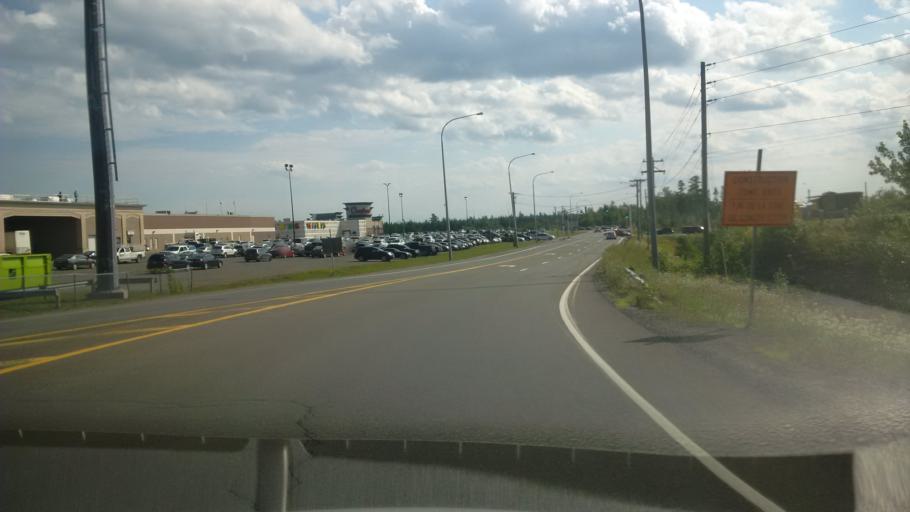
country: CA
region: New Brunswick
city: Fredericton
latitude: 45.9379
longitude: -66.6654
